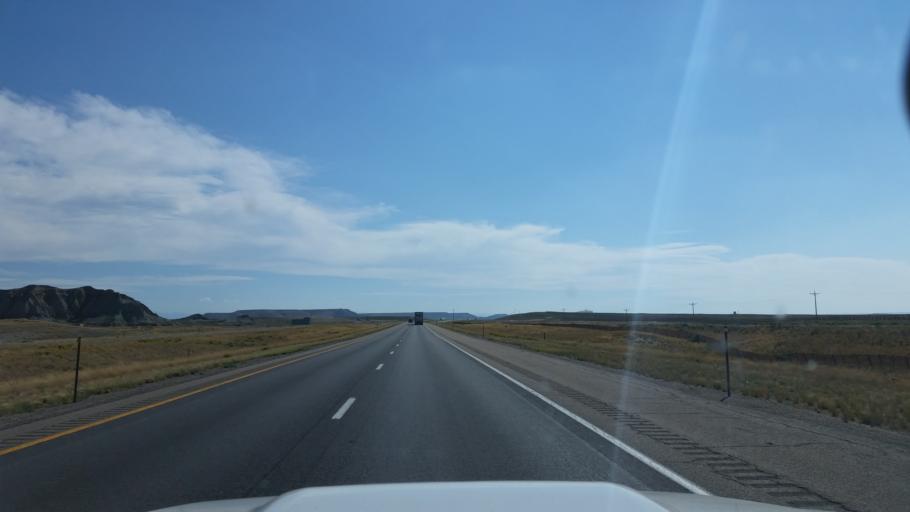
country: US
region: Wyoming
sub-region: Uinta County
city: Lyman
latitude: 41.4761
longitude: -110.0334
